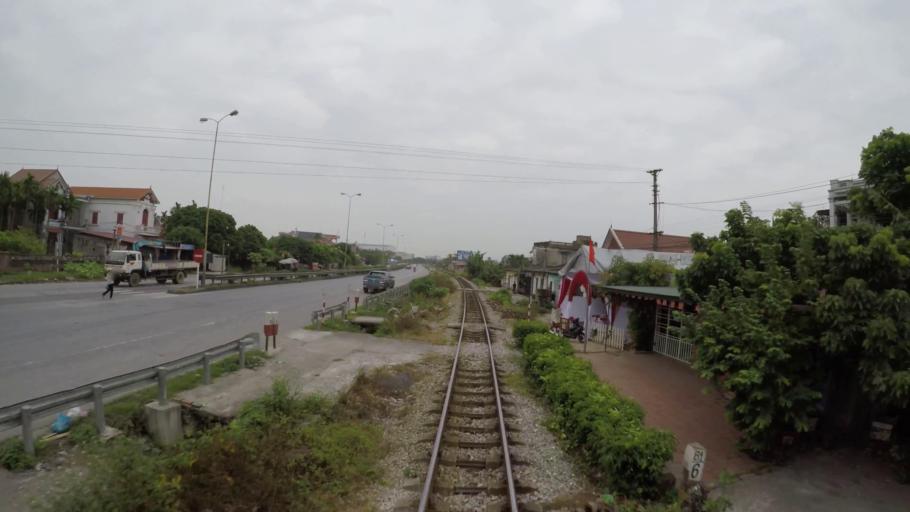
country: VN
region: Hai Duong
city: Phu Thai
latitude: 20.9529
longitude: 106.5306
